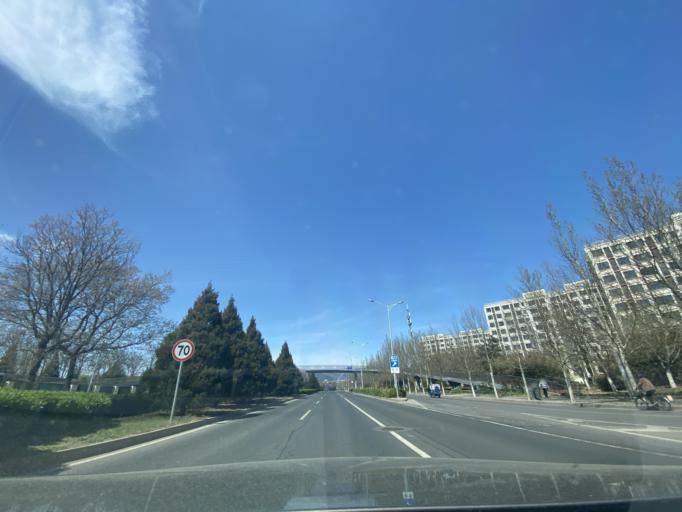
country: CN
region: Beijing
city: Sijiqing
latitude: 39.9347
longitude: 116.2449
